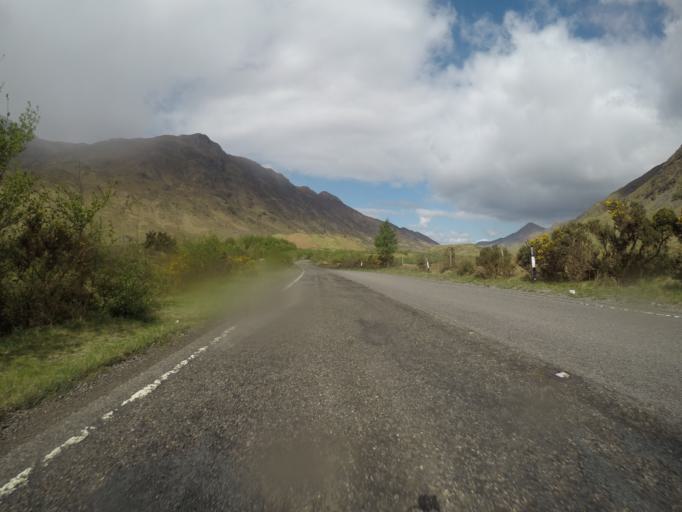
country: GB
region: Scotland
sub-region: Highland
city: Fort William
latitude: 57.1764
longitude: -5.3657
